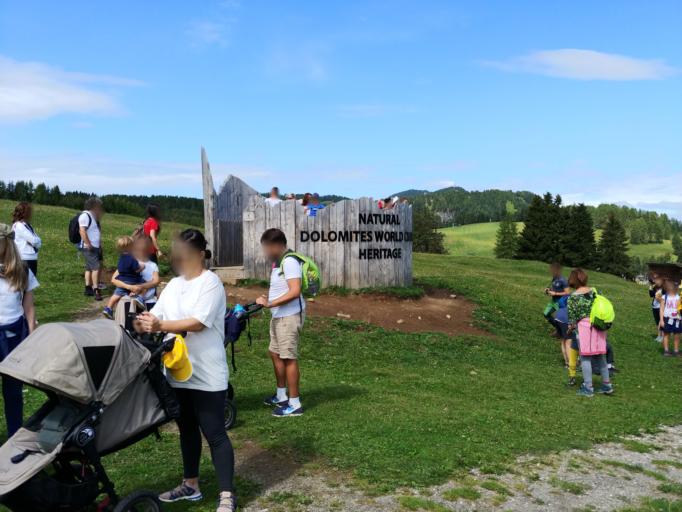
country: IT
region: Trentino-Alto Adige
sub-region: Bolzano
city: Santa Cristina Valgardena
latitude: 46.5494
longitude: 11.7218
